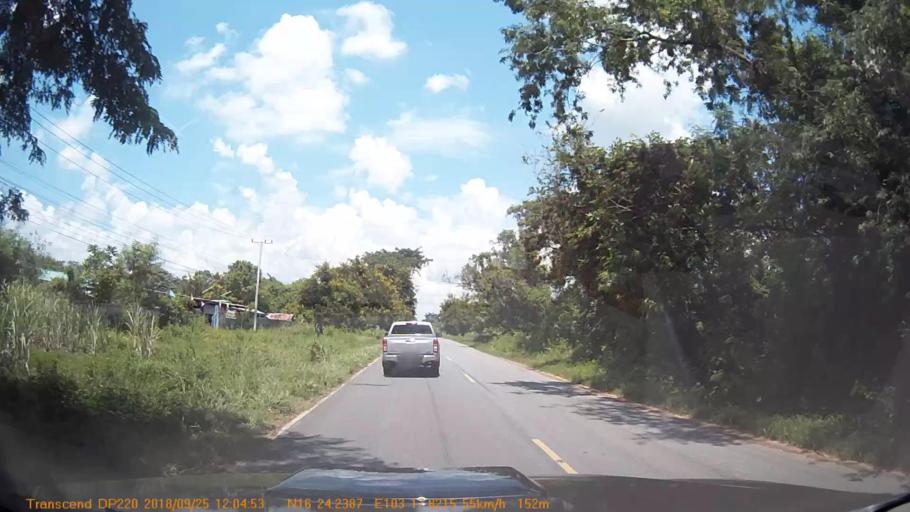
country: TH
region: Kalasin
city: Yang Talat
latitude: 16.4041
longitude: 103.2970
